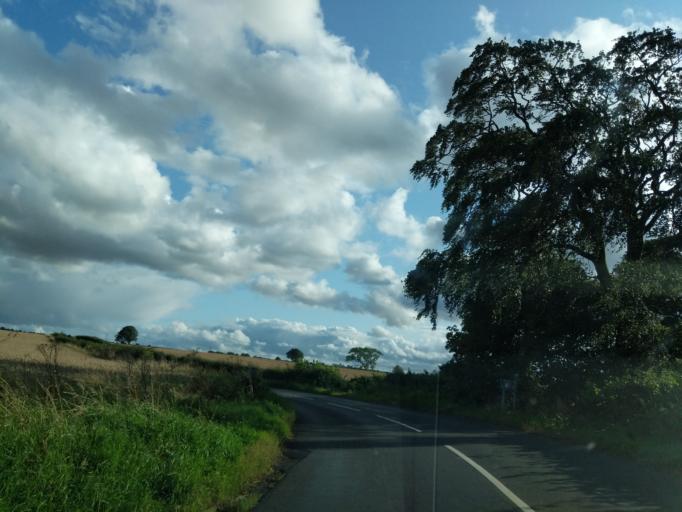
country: GB
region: Scotland
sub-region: East Lothian
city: Longniddry
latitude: 55.9590
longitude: -2.8854
